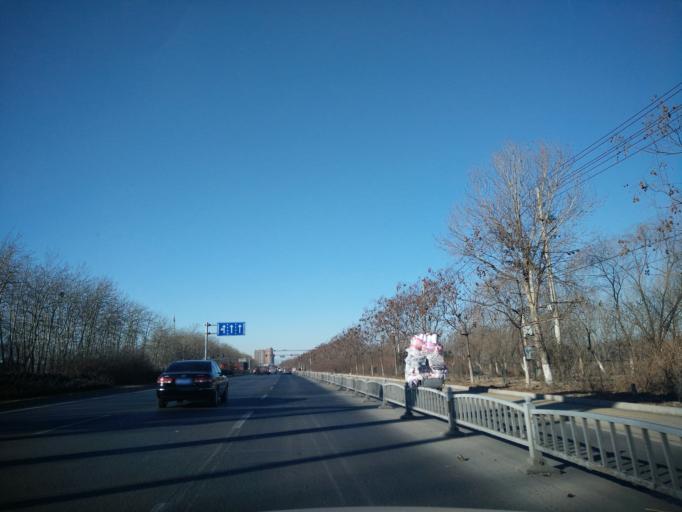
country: CN
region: Beijing
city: Xingfeng
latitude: 39.7209
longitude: 116.3624
